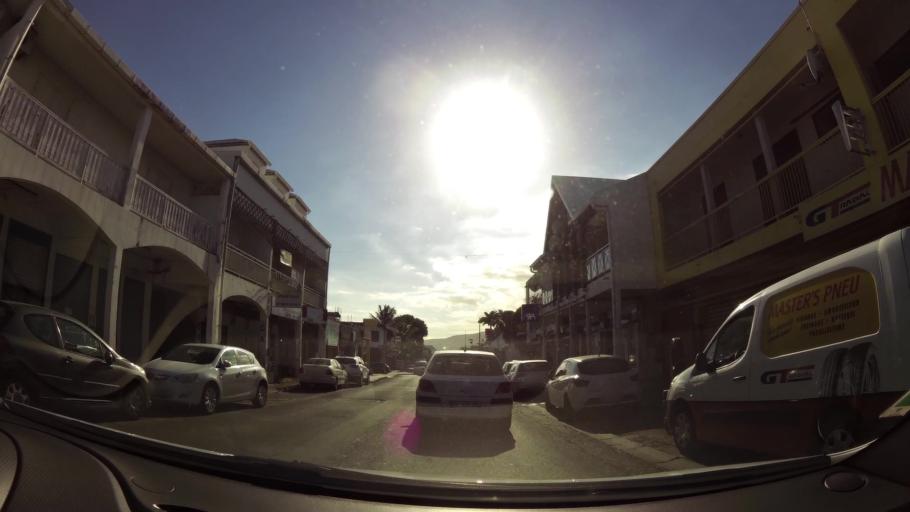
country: RE
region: Reunion
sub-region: Reunion
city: Saint-Louis
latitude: -21.2890
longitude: 55.4113
